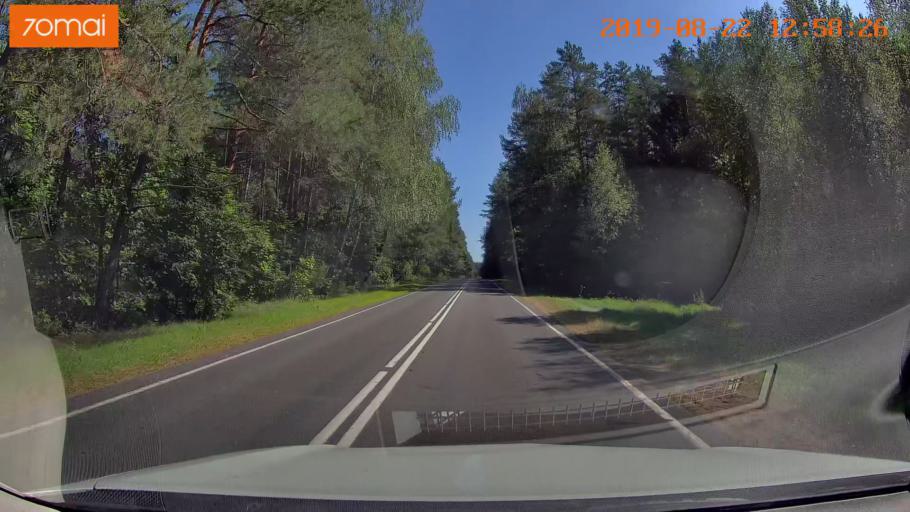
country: BY
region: Minsk
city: Prawdzinski
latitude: 53.4241
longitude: 27.7705
